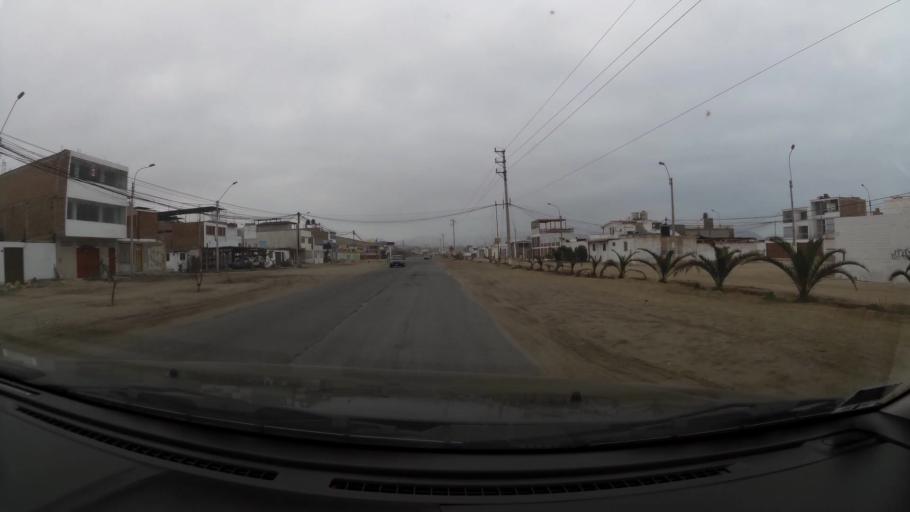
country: PE
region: Lima
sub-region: Lima
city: Punta Hermosa
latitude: -12.3569
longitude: -76.8028
